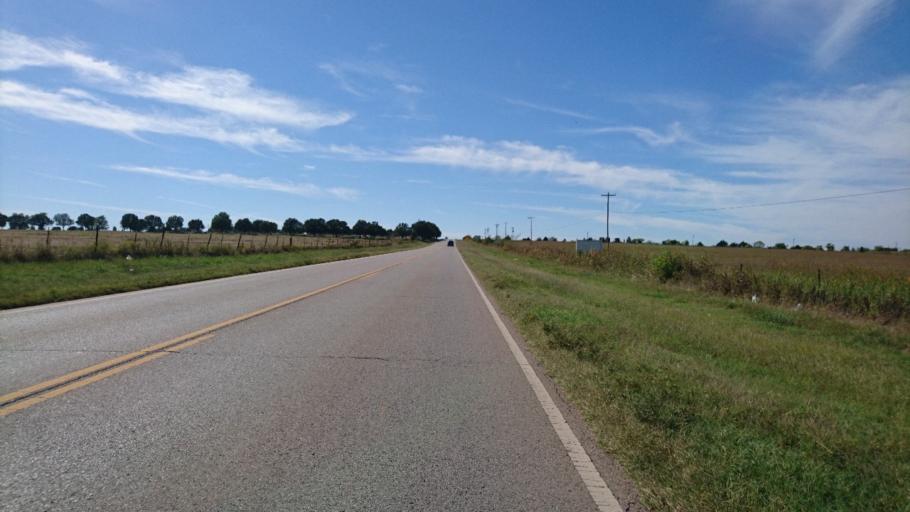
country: US
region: Oklahoma
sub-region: Lincoln County
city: Chandler
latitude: 35.7099
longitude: -96.7823
